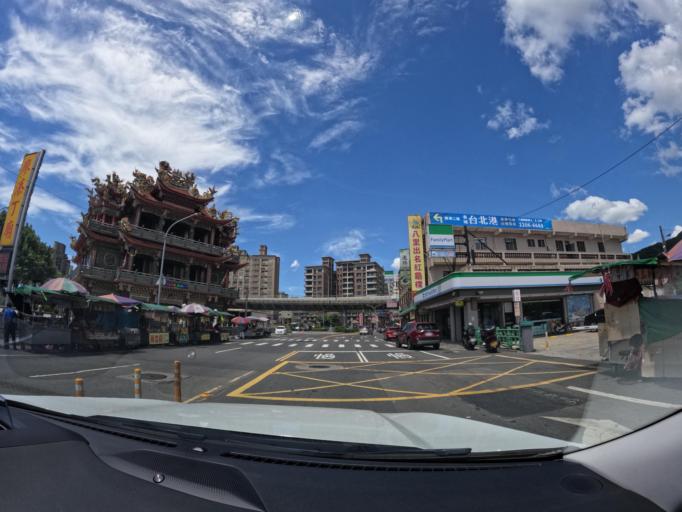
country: TW
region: Taipei
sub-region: Taipei
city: Banqiao
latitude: 25.1432
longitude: 121.3966
